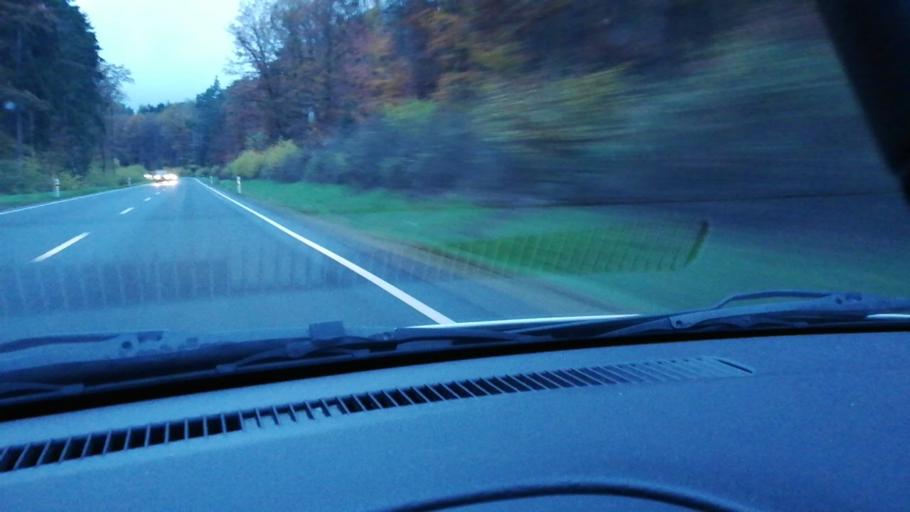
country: DE
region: Bavaria
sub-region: Regierungsbezirk Unterfranken
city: Esselbach
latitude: 49.8555
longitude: 9.5604
